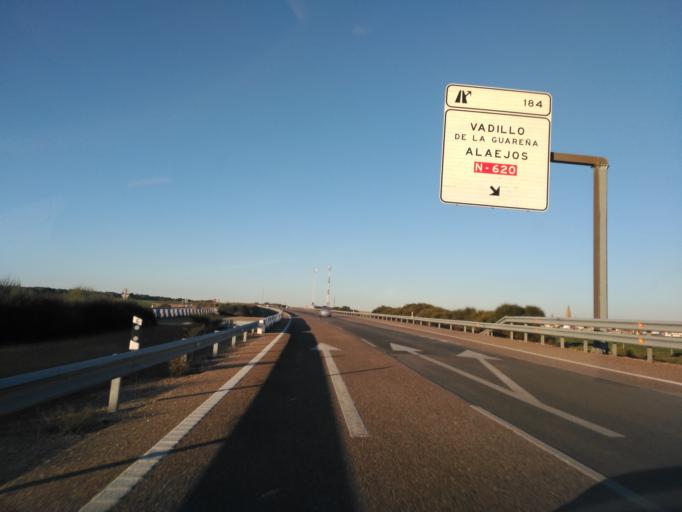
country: ES
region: Castille and Leon
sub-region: Provincia de Valladolid
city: Alaejos
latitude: 41.2983
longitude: -5.2315
